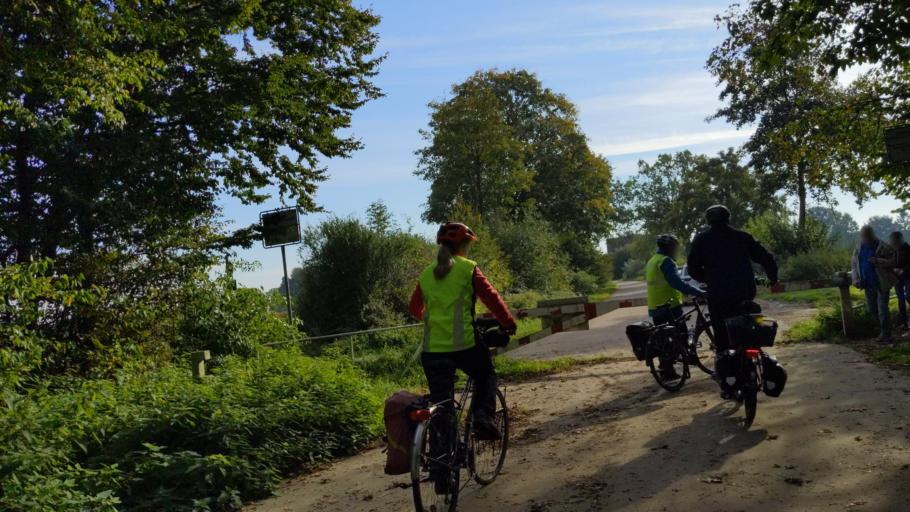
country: DE
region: Schleswig-Holstein
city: Badendorf
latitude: 53.8747
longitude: 10.5867
